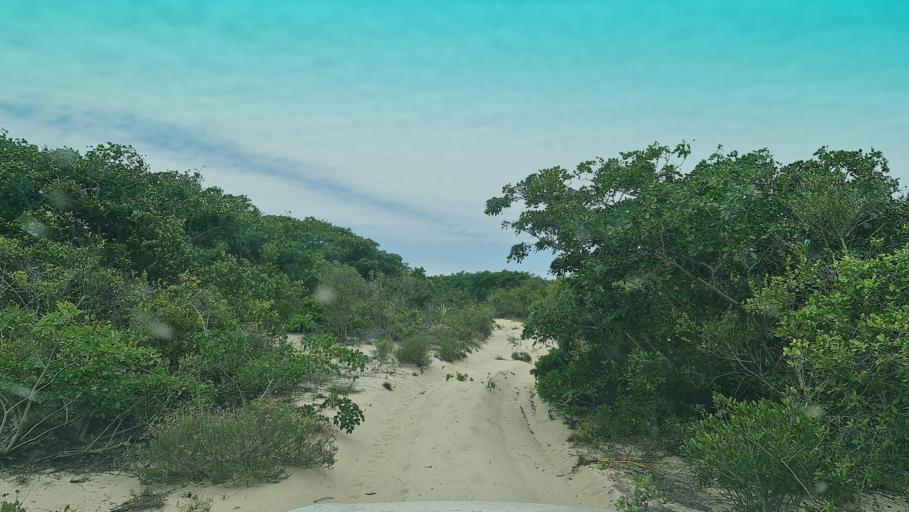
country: MZ
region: Maputo
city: Manhica
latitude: -25.6307
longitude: 32.7881
